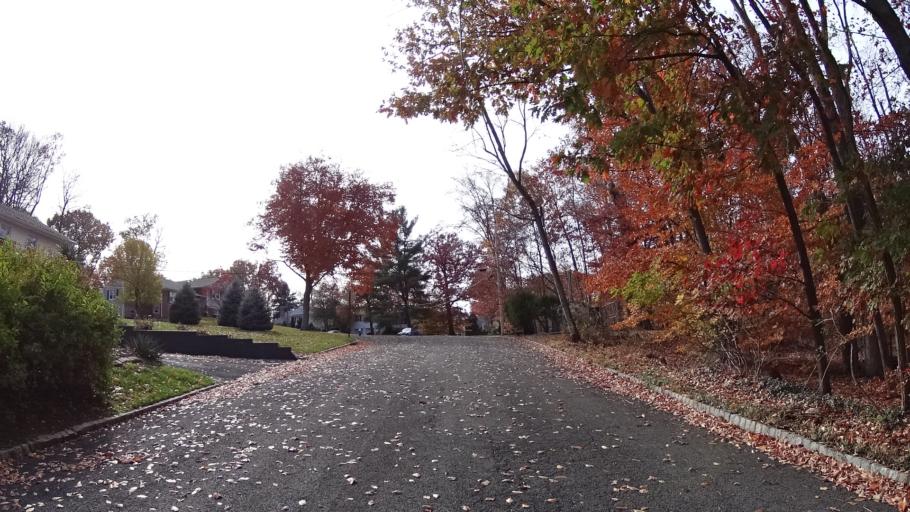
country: US
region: New Jersey
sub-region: Union County
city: New Providence
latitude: 40.7169
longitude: -74.3941
